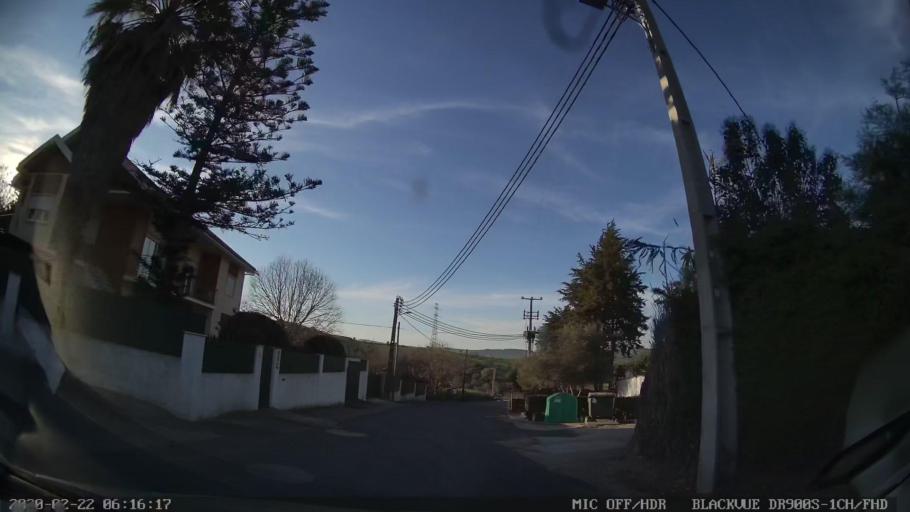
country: PT
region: Lisbon
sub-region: Vila Franca de Xira
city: Castanheira do Ribatejo
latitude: 38.9898
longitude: -9.0166
